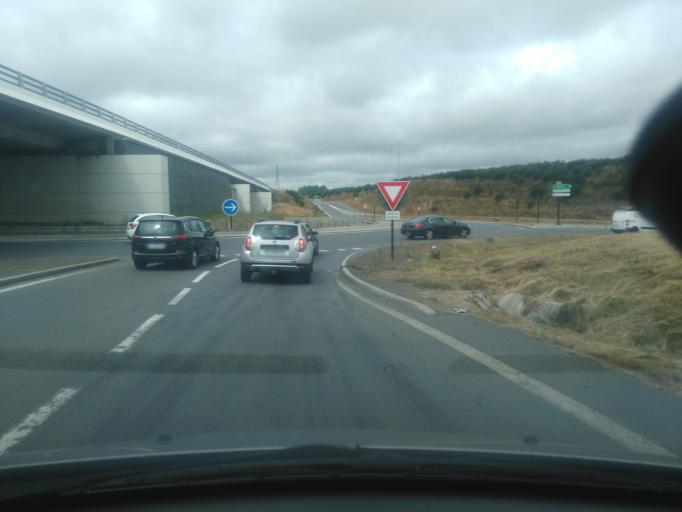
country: FR
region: Brittany
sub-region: Departement des Cotes-d'Armor
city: Ploufragan
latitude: 48.4784
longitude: -2.7671
